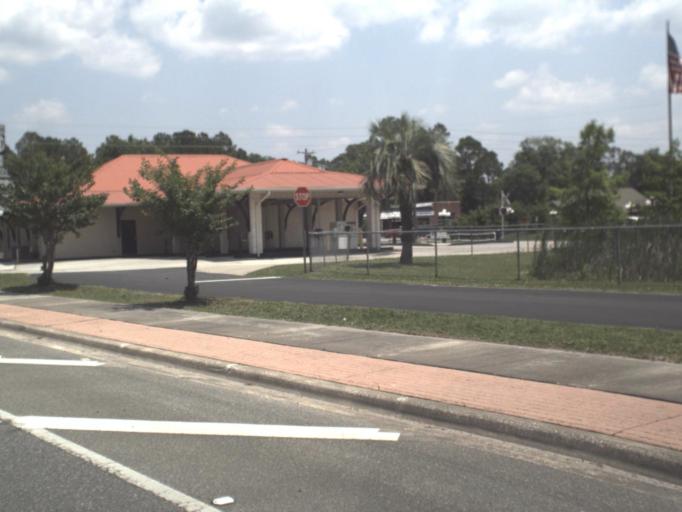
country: US
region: Florida
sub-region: Duval County
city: Baldwin
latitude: 30.3018
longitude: -81.9832
